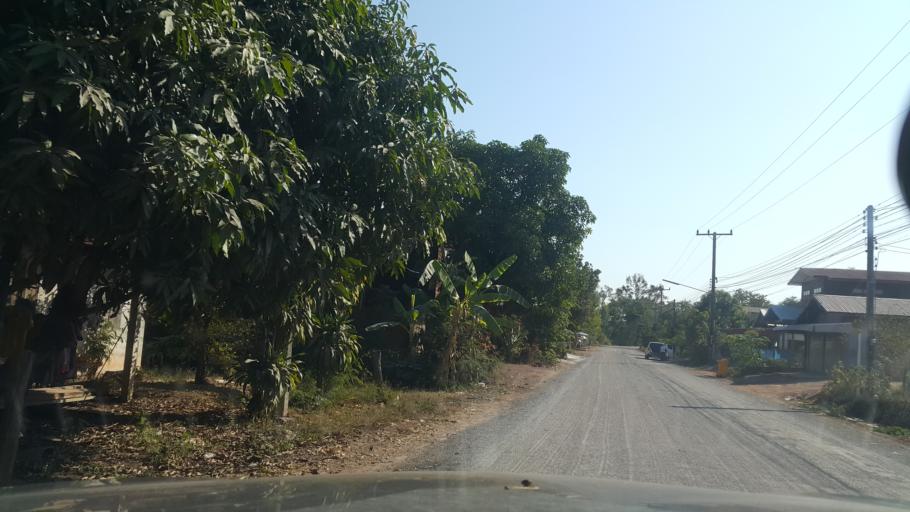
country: TH
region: Changwat Udon Thani
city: Ban Dung
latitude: 17.6785
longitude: 103.3929
